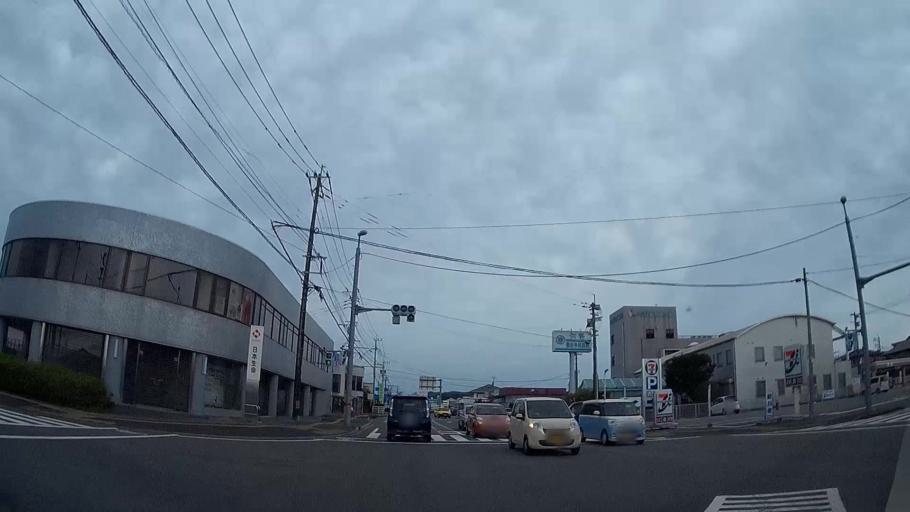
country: JP
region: Kumamoto
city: Kikuchi
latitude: 32.9747
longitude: 130.8084
